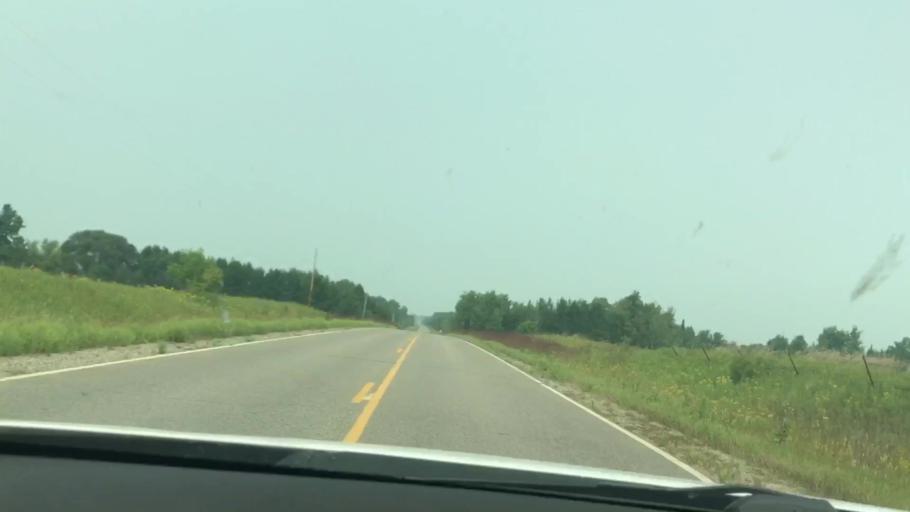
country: US
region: Minnesota
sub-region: Itasca County
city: Cohasset
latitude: 47.3771
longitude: -93.8803
